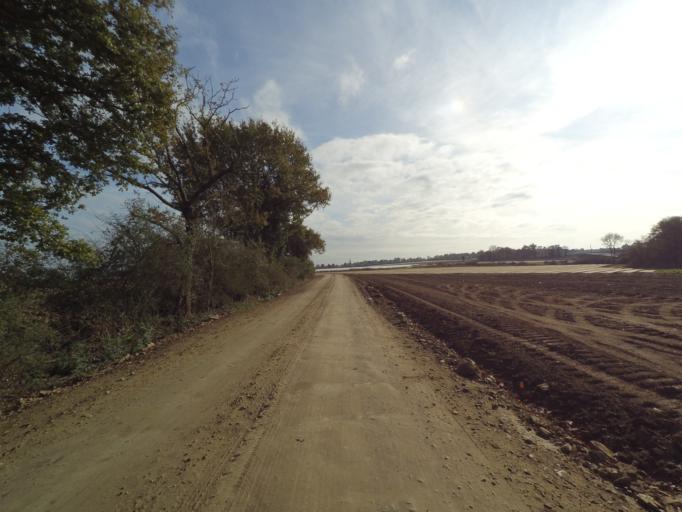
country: FR
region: Pays de la Loire
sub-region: Departement de la Vendee
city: Saint-Hilaire-de-Loulay
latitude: 47.0061
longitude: -1.3623
